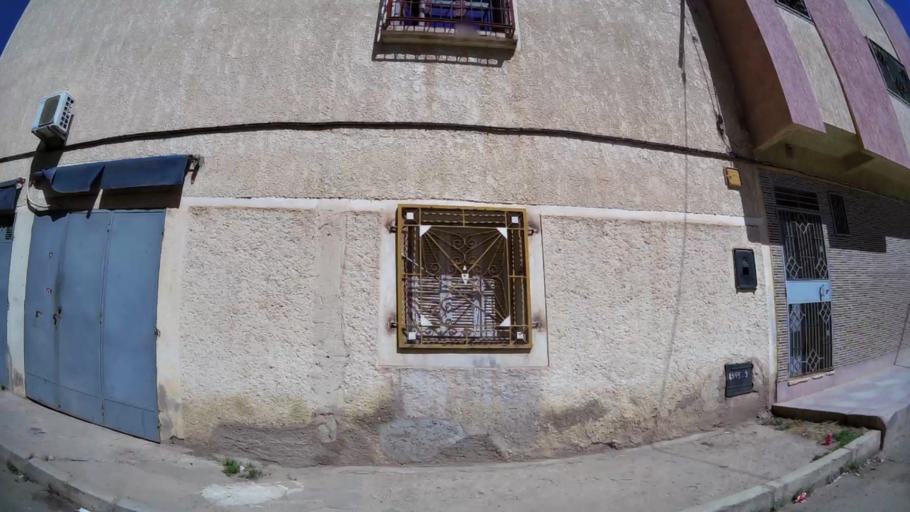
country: MA
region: Oriental
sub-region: Oujda-Angad
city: Oujda
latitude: 34.6852
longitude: -1.9371
